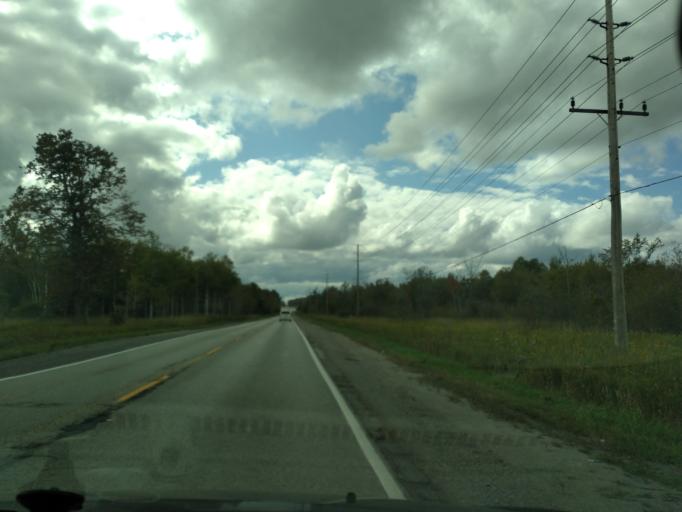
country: CA
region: Ontario
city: Innisfil
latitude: 44.2950
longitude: -79.6360
